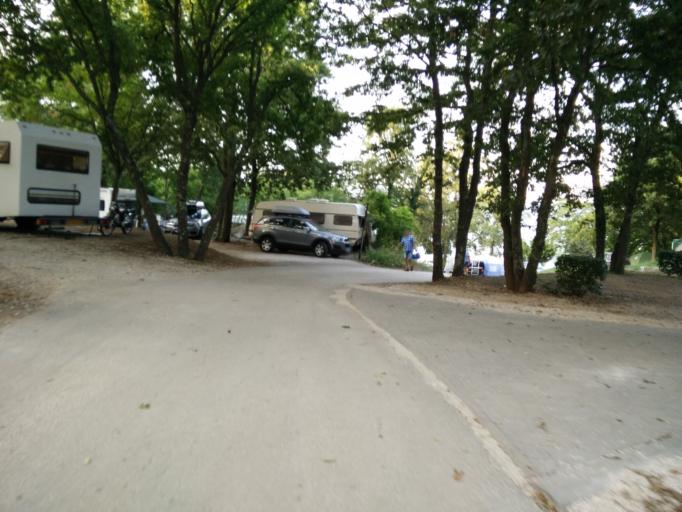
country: HR
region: Istarska
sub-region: Grad Porec
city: Porec
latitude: 45.1907
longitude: 13.5911
